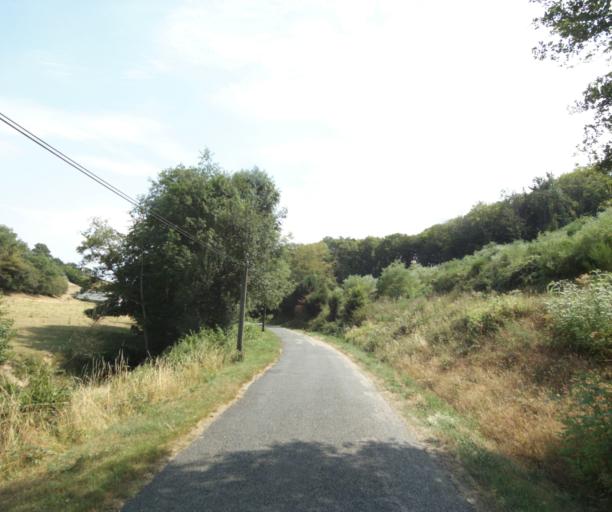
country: FR
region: Bourgogne
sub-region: Departement de Saone-et-Loire
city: Gueugnon
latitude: 46.6168
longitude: 4.0290
